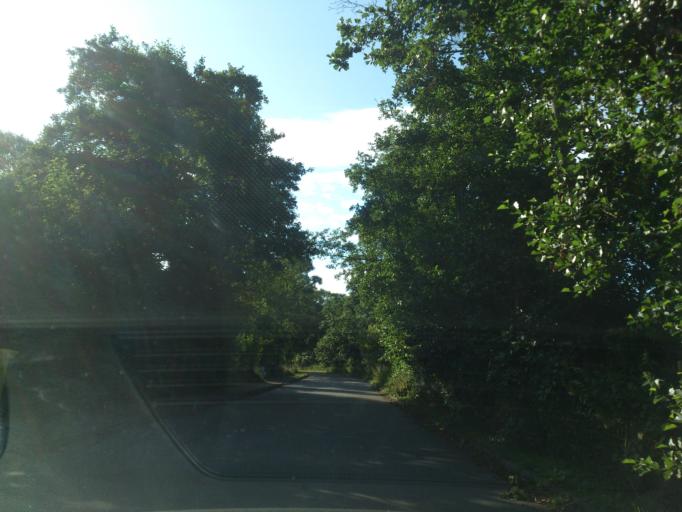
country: DE
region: Schleswig-Holstein
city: Sankt Peter-Ording
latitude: 54.3186
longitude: 8.6193
